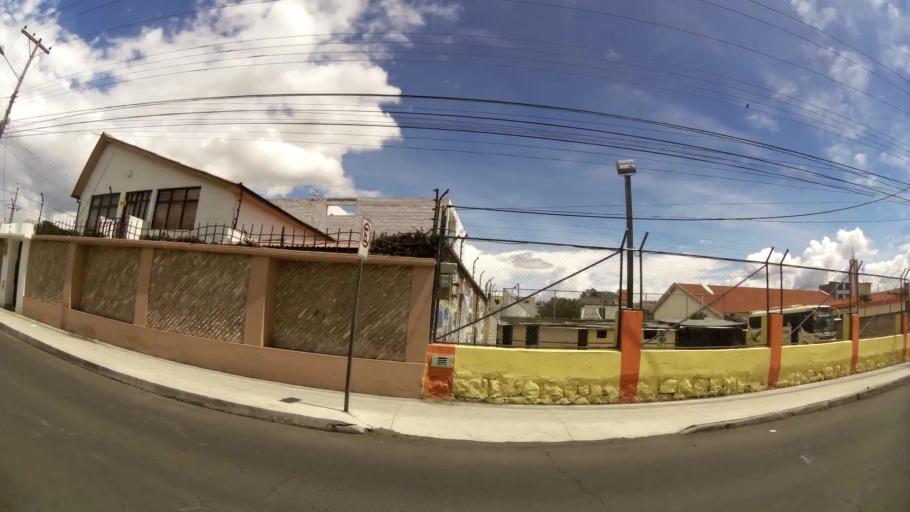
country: EC
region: Tungurahua
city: Ambato
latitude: -1.2490
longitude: -78.6295
